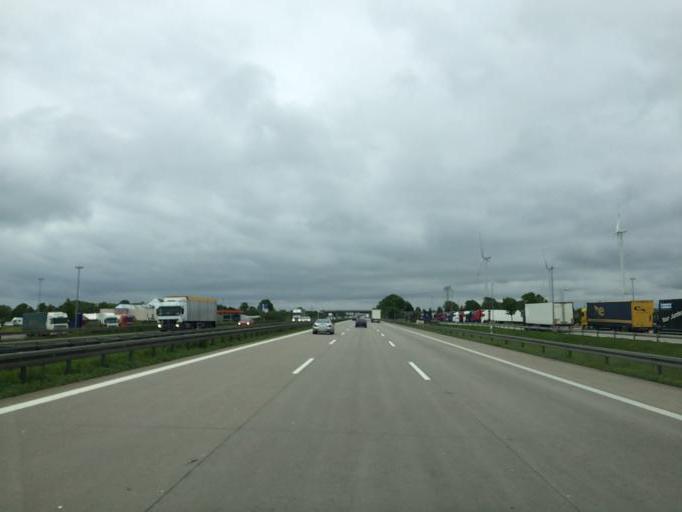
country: DE
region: Saxony-Anhalt
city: Gross Santersleben
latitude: 52.1848
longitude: 11.4502
